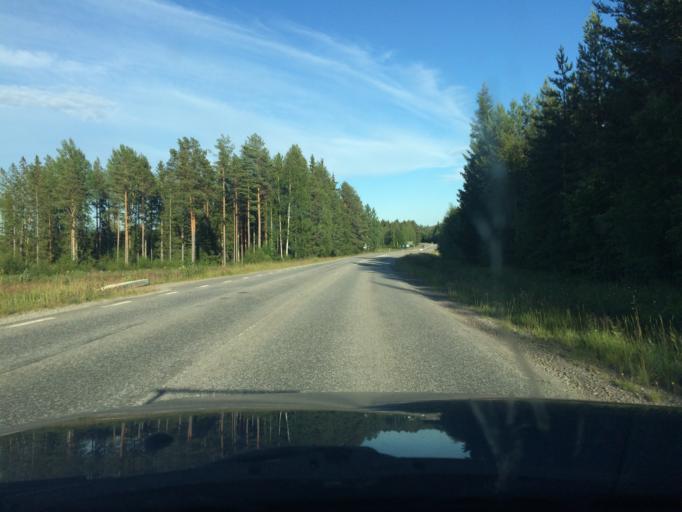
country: SE
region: Norrbotten
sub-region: Pitea Kommun
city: Roknas
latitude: 65.3186
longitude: 21.2866
